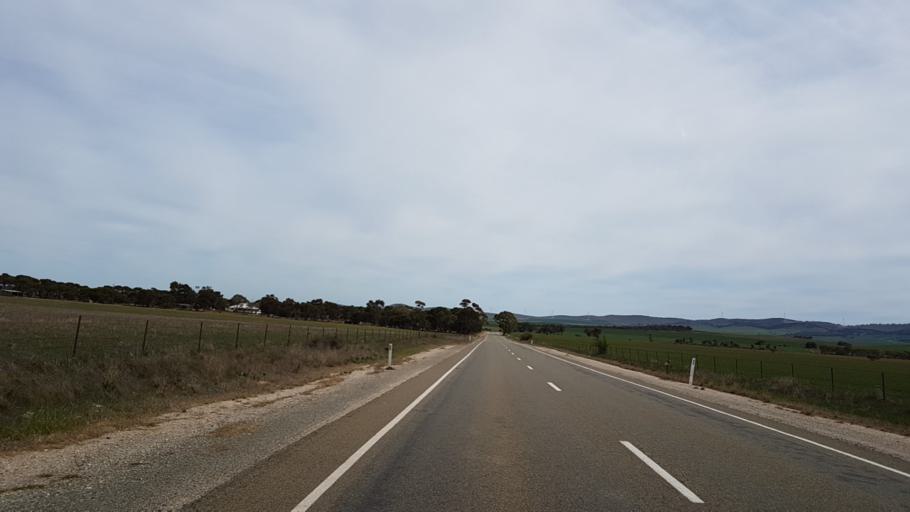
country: AU
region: South Australia
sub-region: Peterborough
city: Peterborough
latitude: -33.0273
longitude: 138.6685
